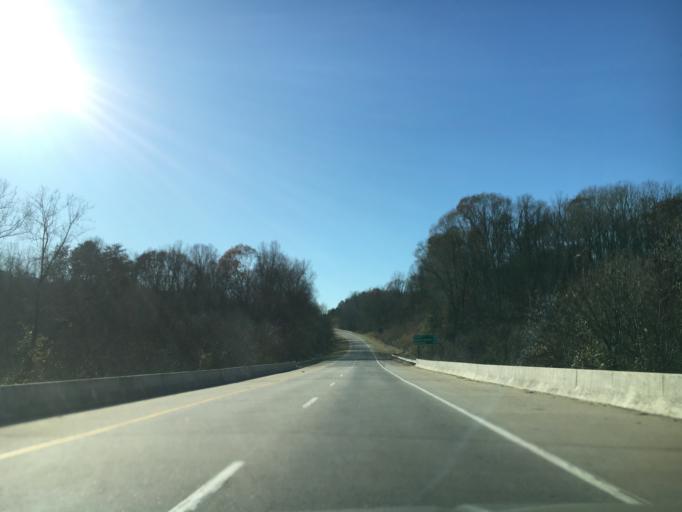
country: US
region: Virginia
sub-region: Henry County
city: Chatmoss
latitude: 36.6389
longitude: -79.8303
